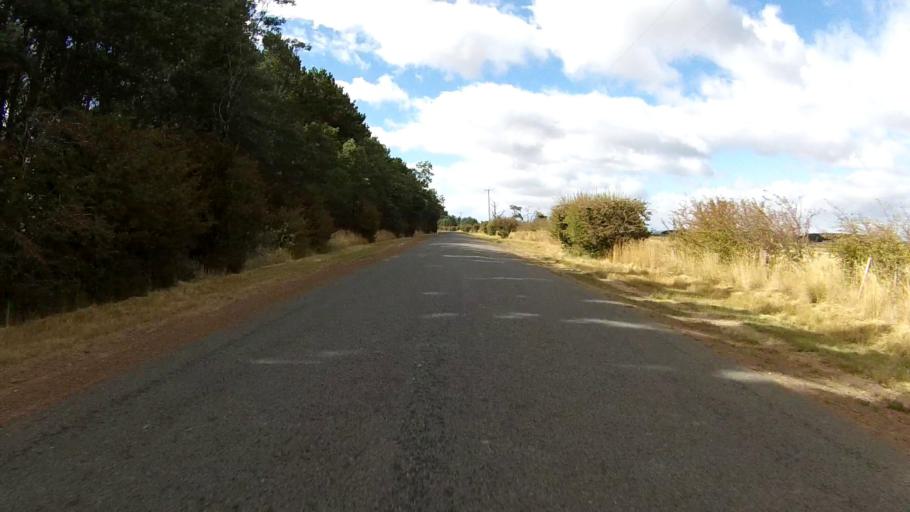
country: AU
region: Tasmania
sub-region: Northern Midlands
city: Evandale
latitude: -41.6807
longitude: 147.3546
